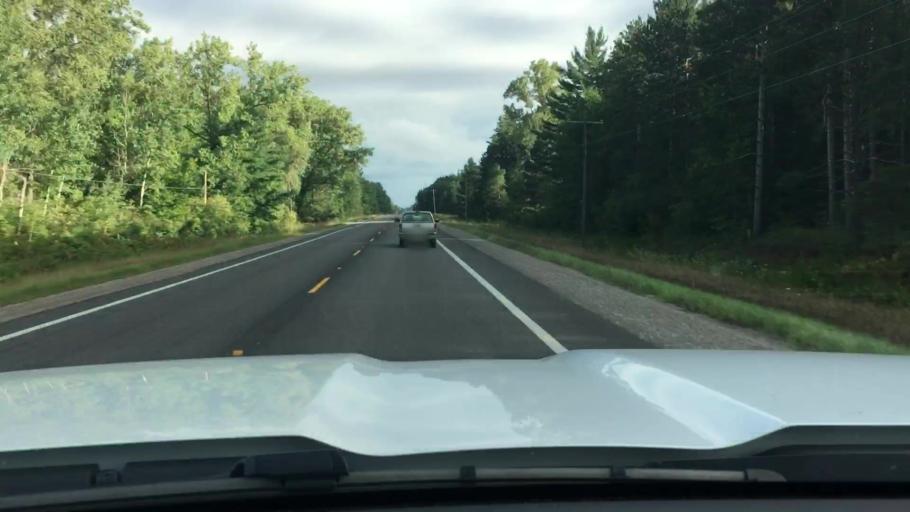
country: US
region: Michigan
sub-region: Tuscola County
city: Caro
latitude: 43.4241
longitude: -83.3845
